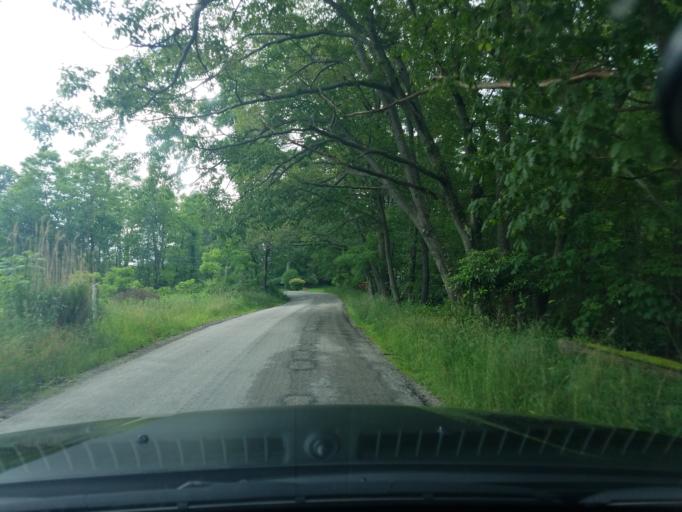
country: US
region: Pennsylvania
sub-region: Westmoreland County
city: Calumet
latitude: 40.1936
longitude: -79.3899
